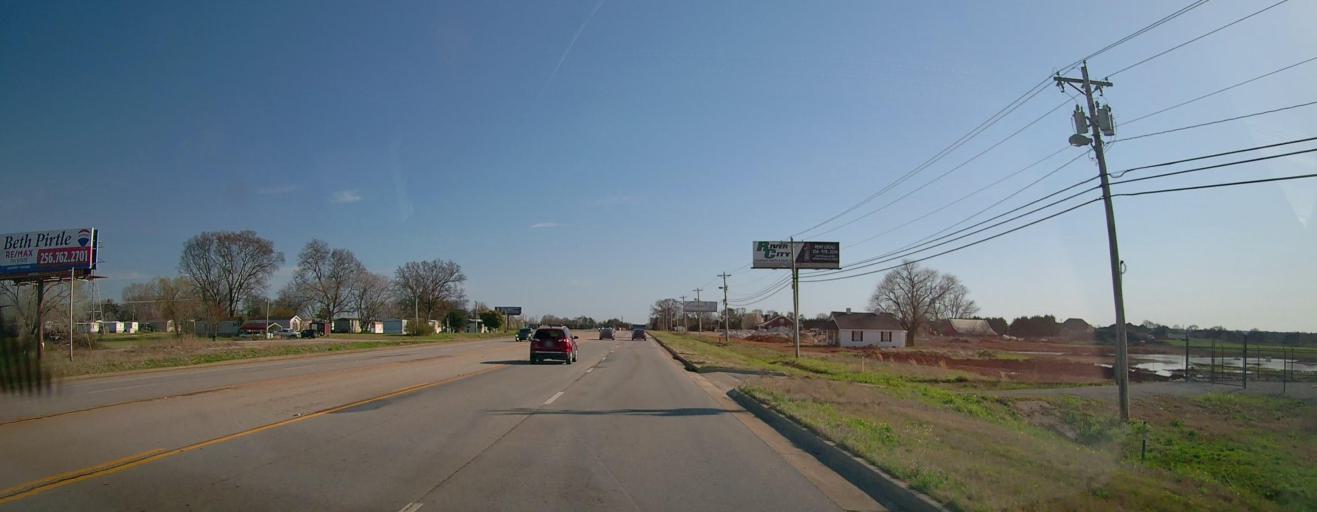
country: US
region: Alabama
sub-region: Colbert County
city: Muscle Shoals
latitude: 34.7221
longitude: -87.6351
